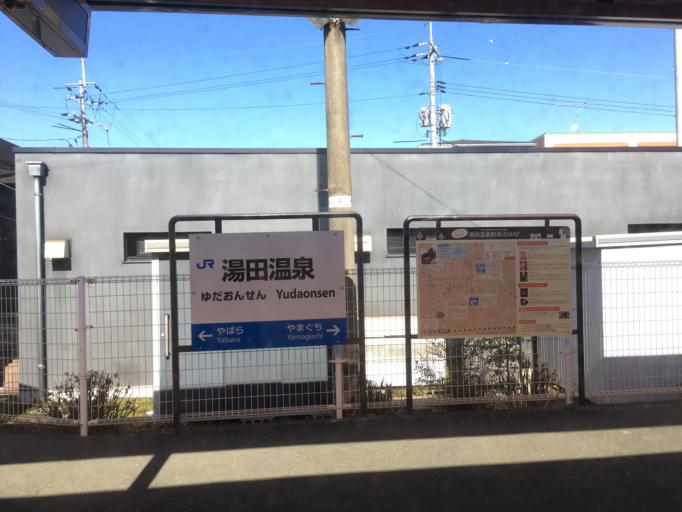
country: JP
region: Yamaguchi
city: Yamaguchi-shi
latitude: 34.1598
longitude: 131.4603
